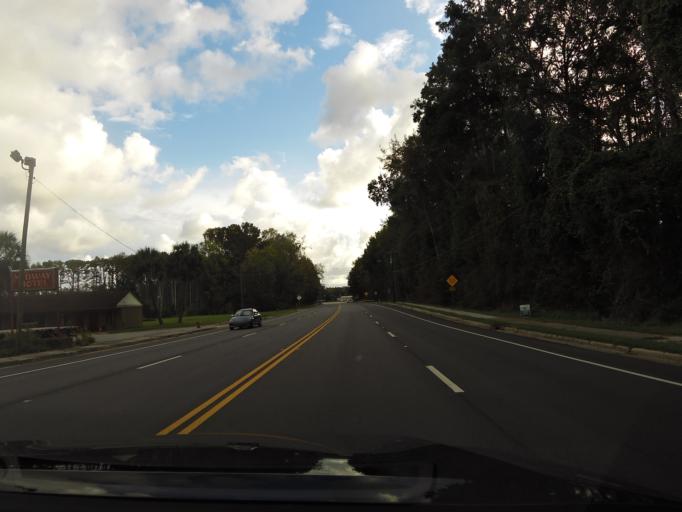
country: US
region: Georgia
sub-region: Liberty County
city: Midway
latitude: 31.8039
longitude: -81.4314
